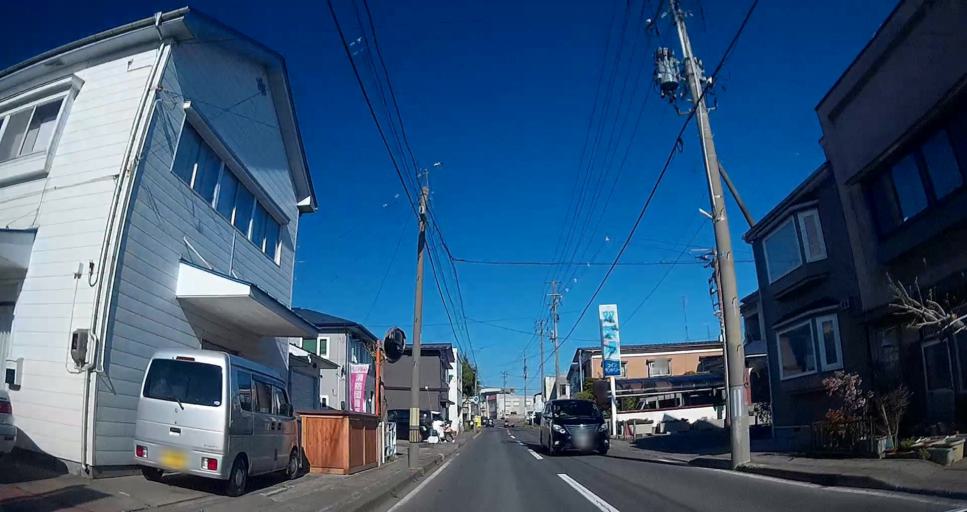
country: JP
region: Aomori
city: Hachinohe
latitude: 40.5238
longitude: 141.5320
